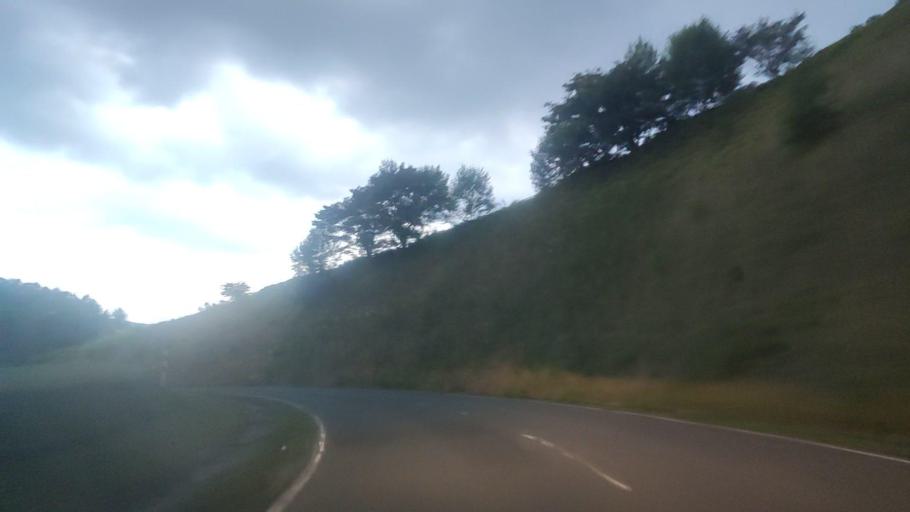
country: JP
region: Hokkaido
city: Shimo-furano
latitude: 43.3600
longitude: 142.3735
